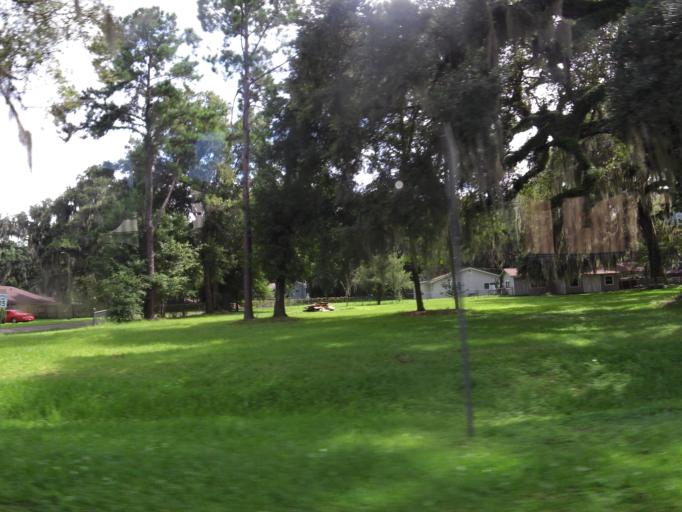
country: US
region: Florida
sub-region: Clay County
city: Lakeside
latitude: 30.1232
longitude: -81.7611
